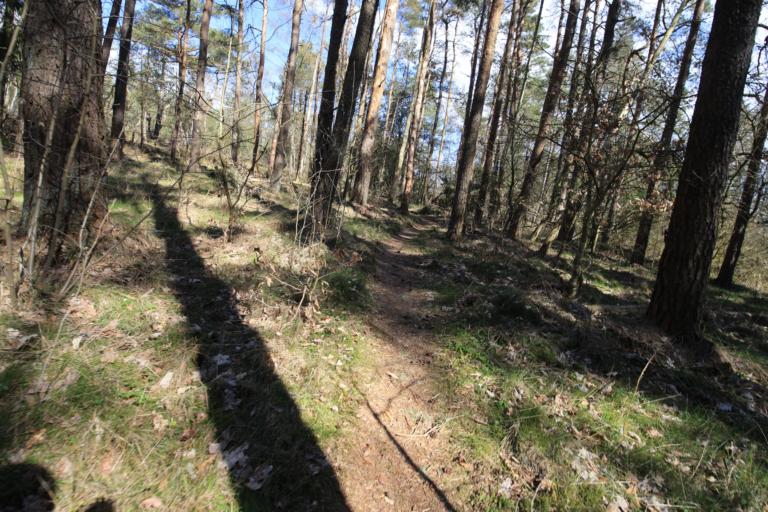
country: SE
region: Halland
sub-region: Varbergs Kommun
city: Varberg
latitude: 57.1778
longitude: 12.2419
